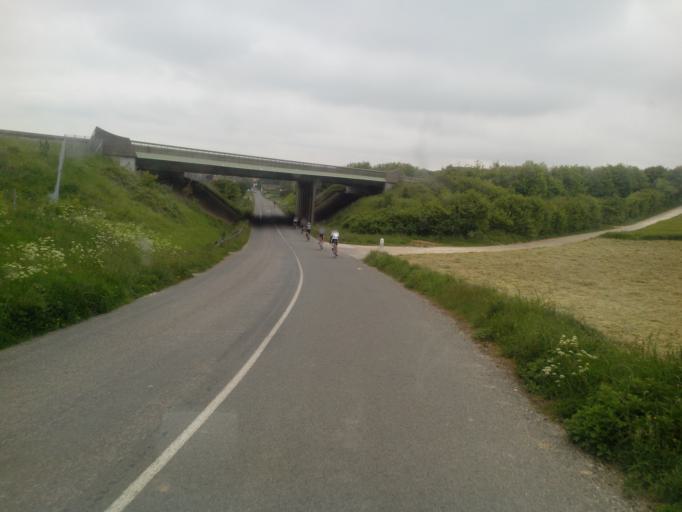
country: FR
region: Nord-Pas-de-Calais
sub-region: Departement du Pas-de-Calais
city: Nesles
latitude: 50.6138
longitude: 1.6576
